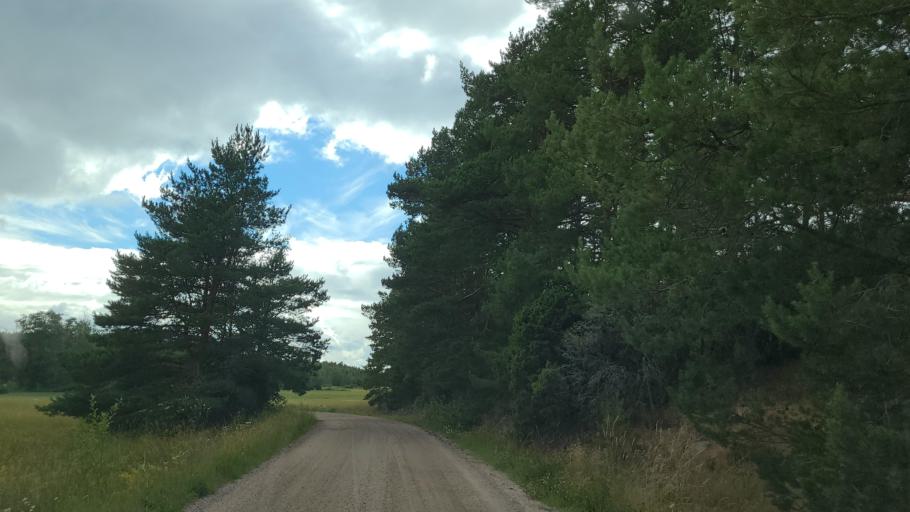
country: FI
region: Varsinais-Suomi
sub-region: Aboland-Turunmaa
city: Nagu
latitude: 60.2050
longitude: 21.8103
